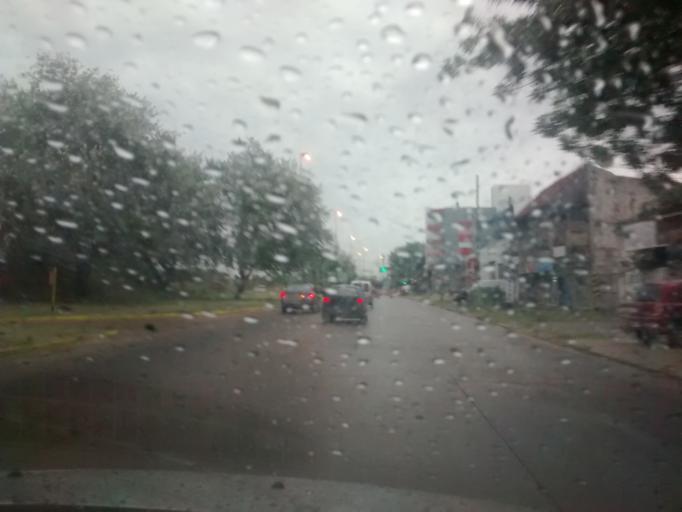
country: AR
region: Buenos Aires
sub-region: Partido de La Plata
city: La Plata
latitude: -34.9289
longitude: -57.9856
